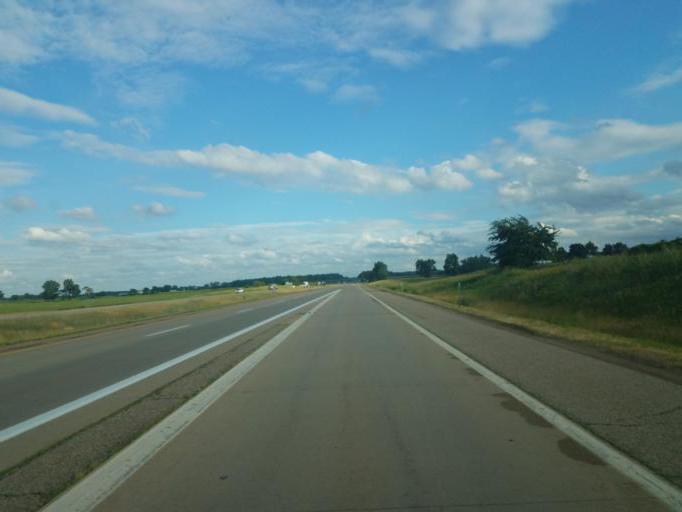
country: US
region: Indiana
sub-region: Steuben County
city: Fremont
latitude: 41.7927
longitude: -84.9943
